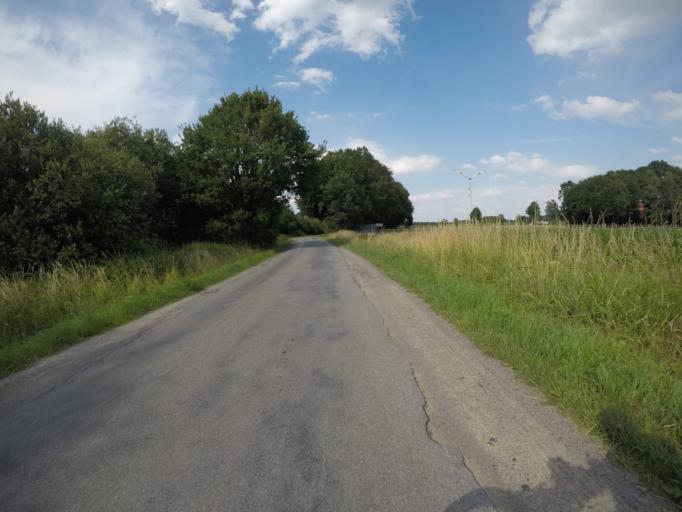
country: DE
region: North Rhine-Westphalia
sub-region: Regierungsbezirk Munster
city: Coesfeld
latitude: 51.9055
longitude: 7.1441
